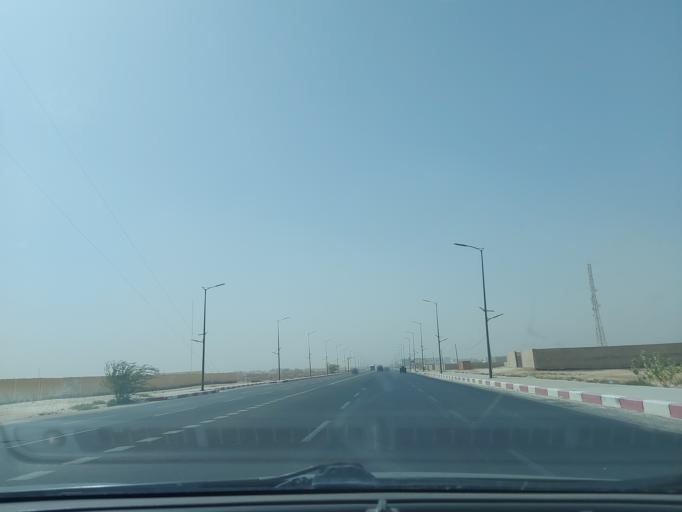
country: MR
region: Nouakchott
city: Nouakchott
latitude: 18.1415
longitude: -16.0065
